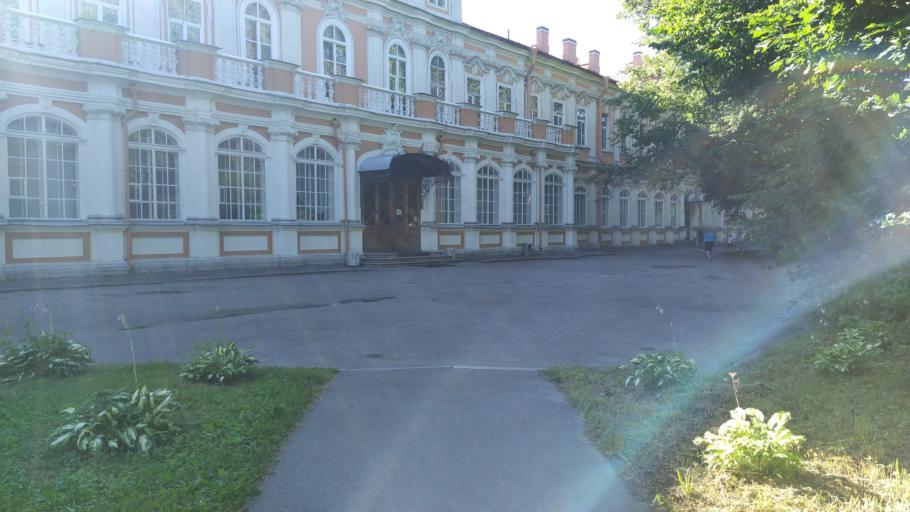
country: RU
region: St.-Petersburg
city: Centralniy
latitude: 59.9205
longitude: 30.3868
